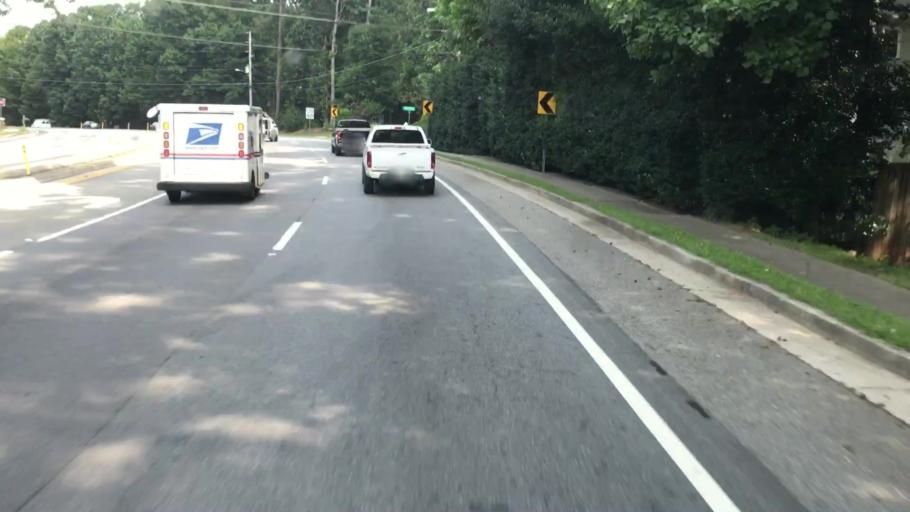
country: US
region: Georgia
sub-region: Gwinnett County
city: Lawrenceville
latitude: 33.9472
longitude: -84.0443
